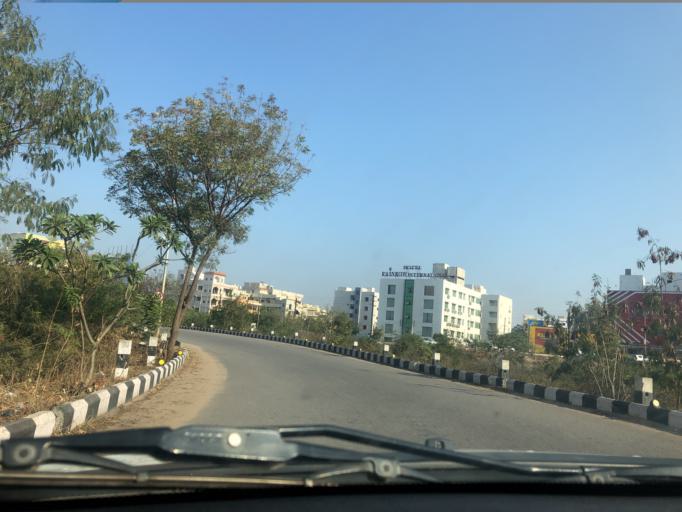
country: IN
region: Telangana
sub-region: Rangareddi
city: Sriramnagar
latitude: 17.2579
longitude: 78.3825
